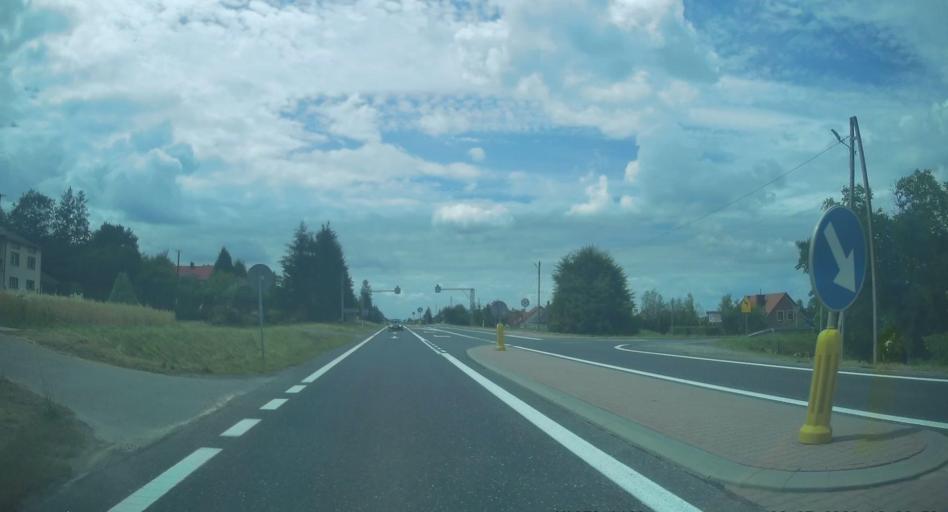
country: PL
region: Subcarpathian Voivodeship
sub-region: Powiat ropczycko-sedziszowski
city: Ostrow
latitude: 50.0620
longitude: 21.5474
